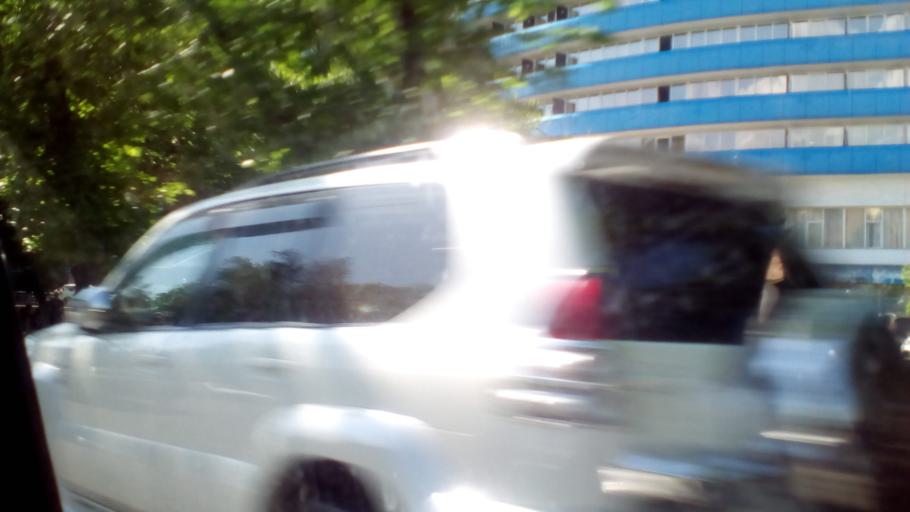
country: KZ
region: Almaty Qalasy
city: Almaty
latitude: 43.2498
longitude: 76.9457
